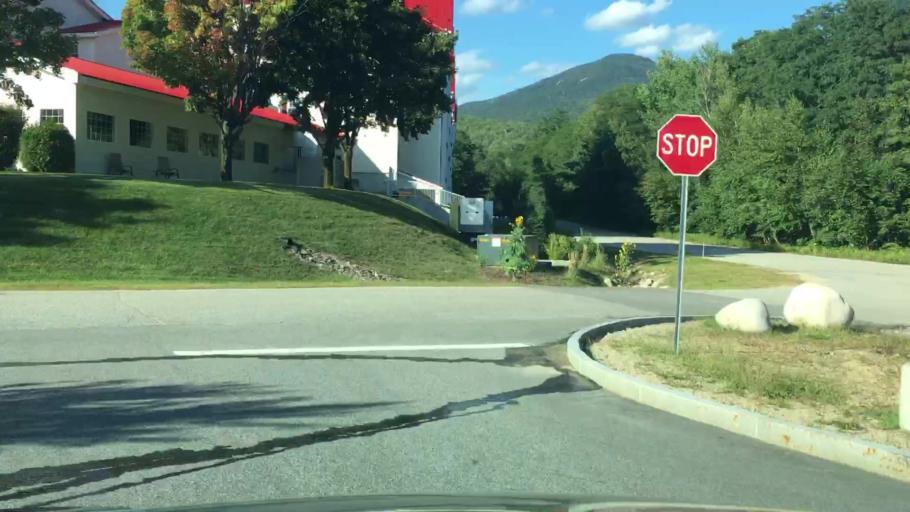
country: US
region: New Hampshire
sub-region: Grafton County
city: Woodstock
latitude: 44.0430
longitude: -71.6672
